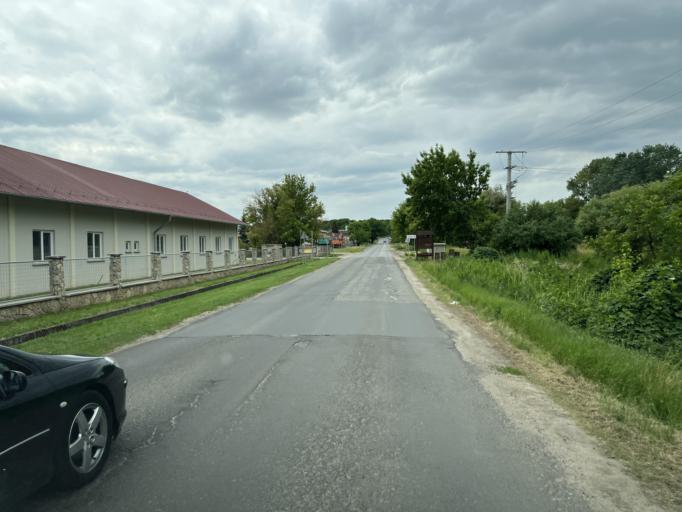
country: HU
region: Pest
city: Nagytarcsa
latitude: 47.5414
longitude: 19.2761
